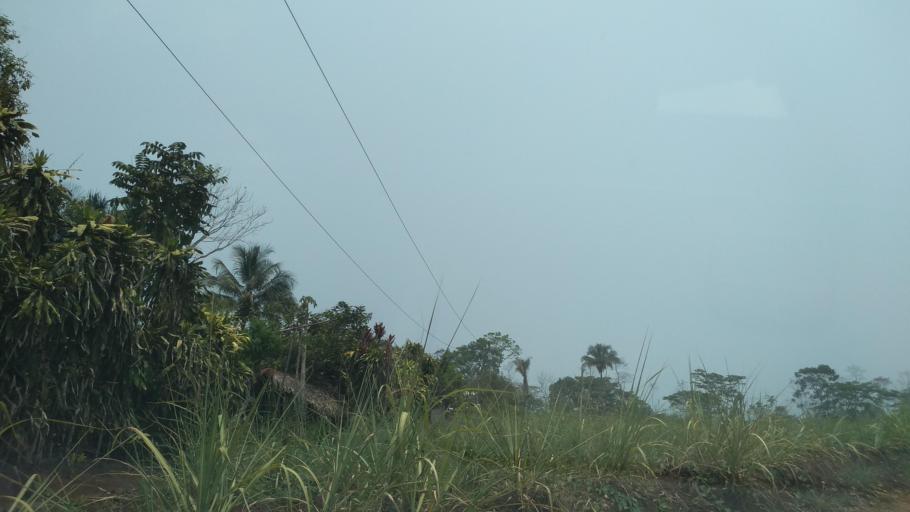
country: MX
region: Puebla
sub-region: San Sebastian Tlacotepec
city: San Martin Mazateopan
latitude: 18.4969
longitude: -96.7800
